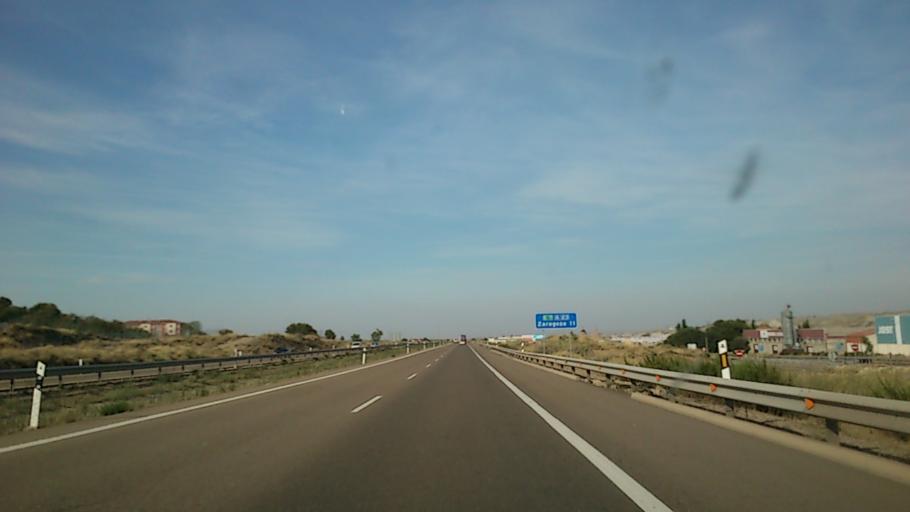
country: ES
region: Aragon
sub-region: Provincia de Zaragoza
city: Cadrete
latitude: 41.5624
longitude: -0.9692
